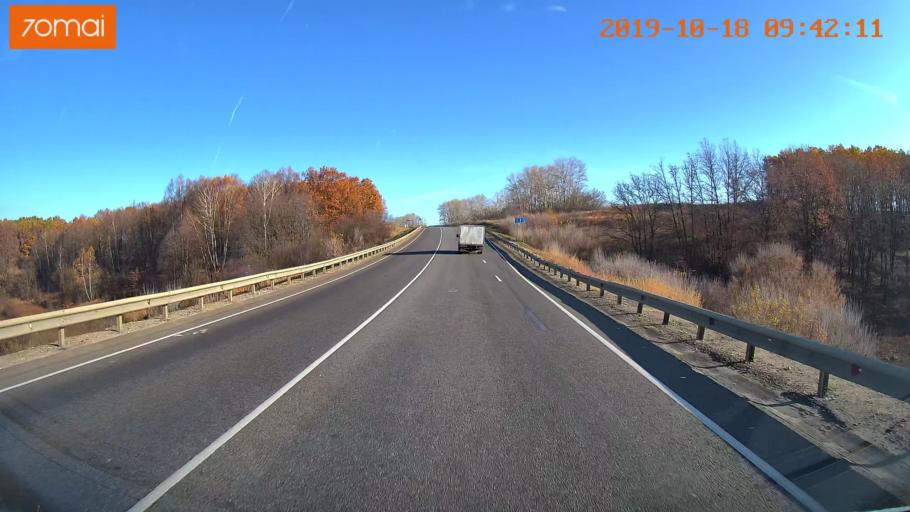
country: RU
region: Tula
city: Kazachka
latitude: 53.2840
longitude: 38.1731
